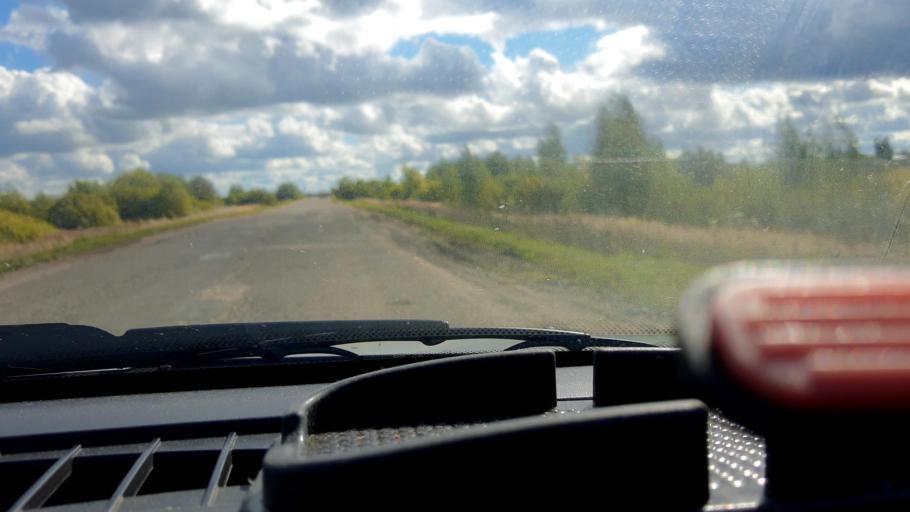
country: RU
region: Nizjnij Novgorod
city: Sharanga
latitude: 56.9405
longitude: 46.6471
